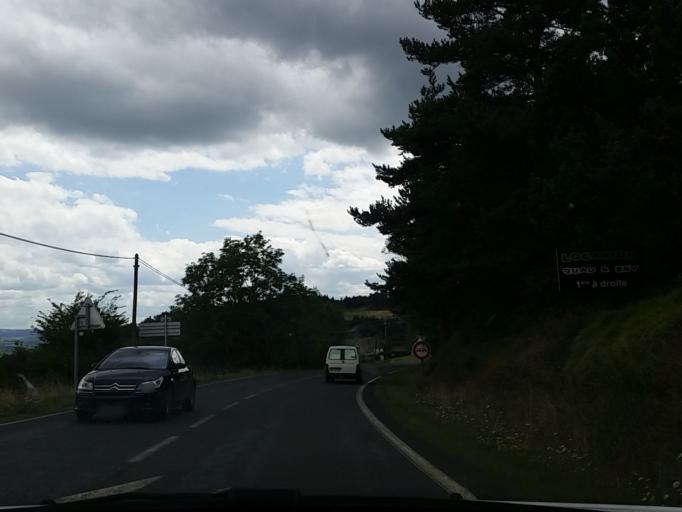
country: FR
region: Auvergne
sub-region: Departement du Cantal
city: Neuveglise
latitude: 44.9310
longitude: 2.9982
